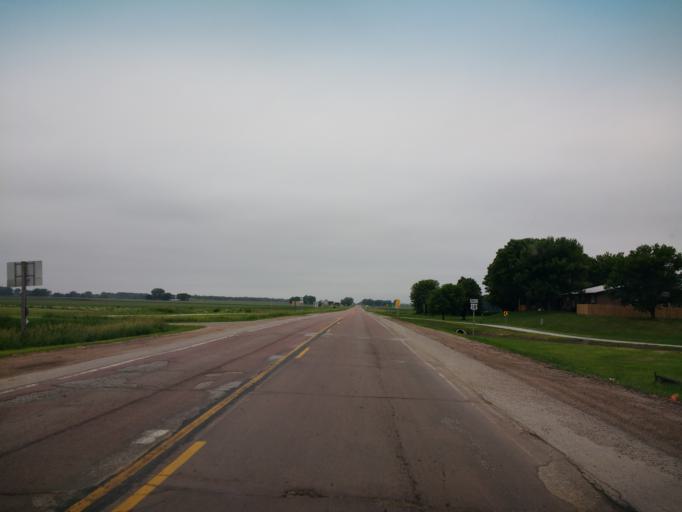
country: US
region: Iowa
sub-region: Clay County
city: Spencer
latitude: 43.1841
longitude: -95.1510
